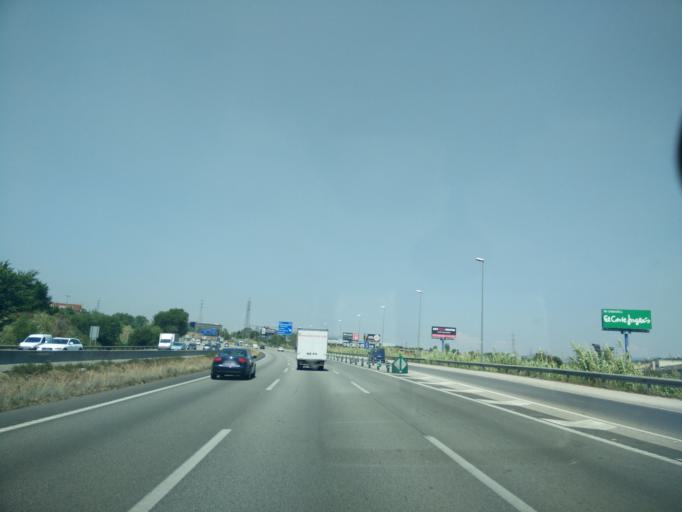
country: ES
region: Catalonia
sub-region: Provincia de Barcelona
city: Cerdanyola del Valles
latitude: 41.5010
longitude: 2.1453
